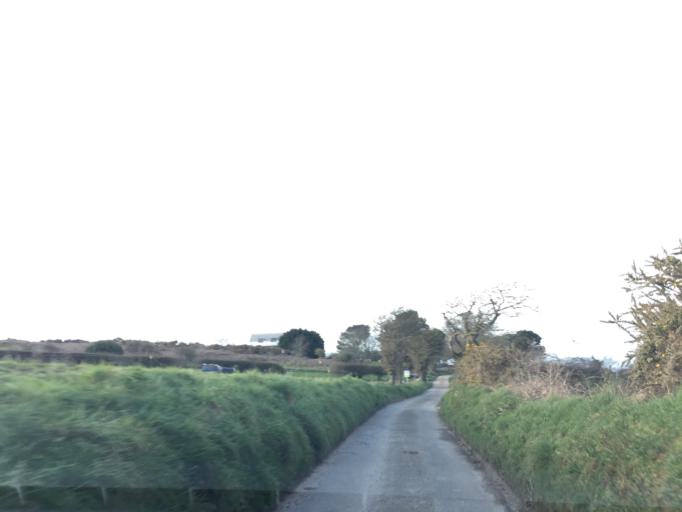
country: JE
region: St Helier
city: Saint Helier
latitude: 49.2463
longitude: -2.0983
